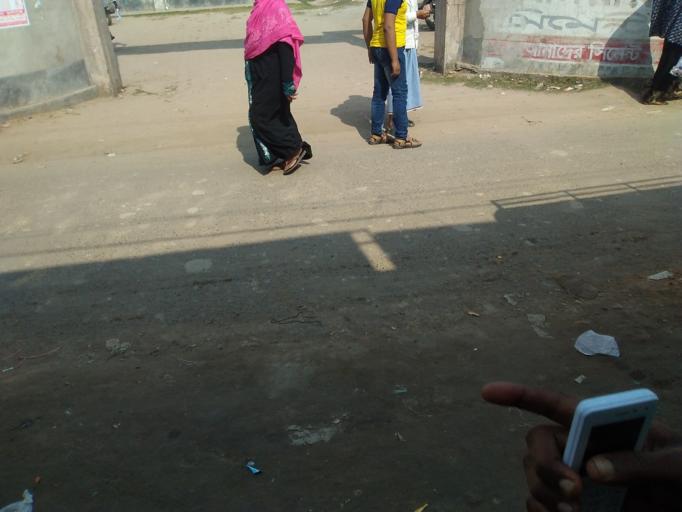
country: IN
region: West Bengal
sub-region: North 24 Parganas
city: Taki
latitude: 22.6403
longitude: 88.9871
